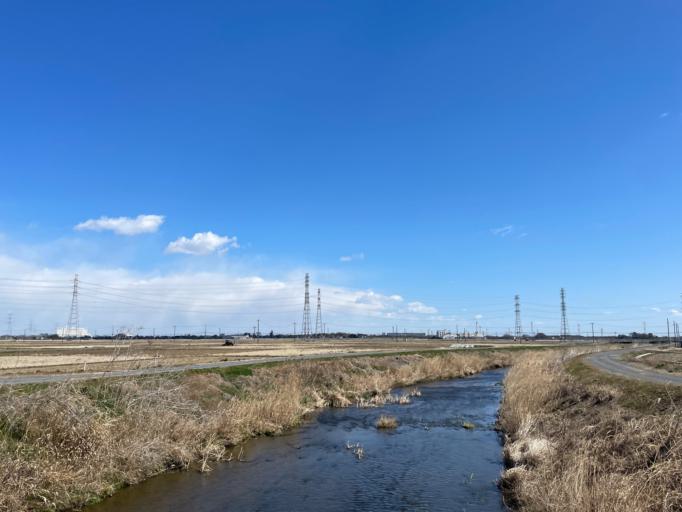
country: JP
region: Saitama
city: Sakado
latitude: 35.9797
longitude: 139.4157
